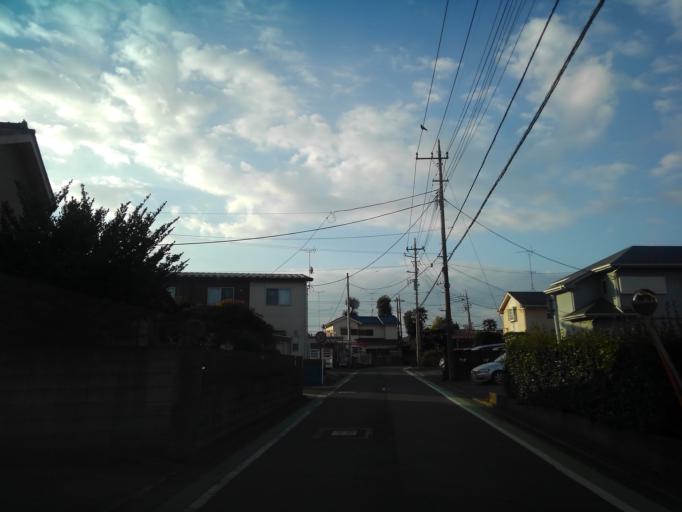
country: JP
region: Saitama
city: Tokorozawa
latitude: 35.7904
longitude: 139.4239
